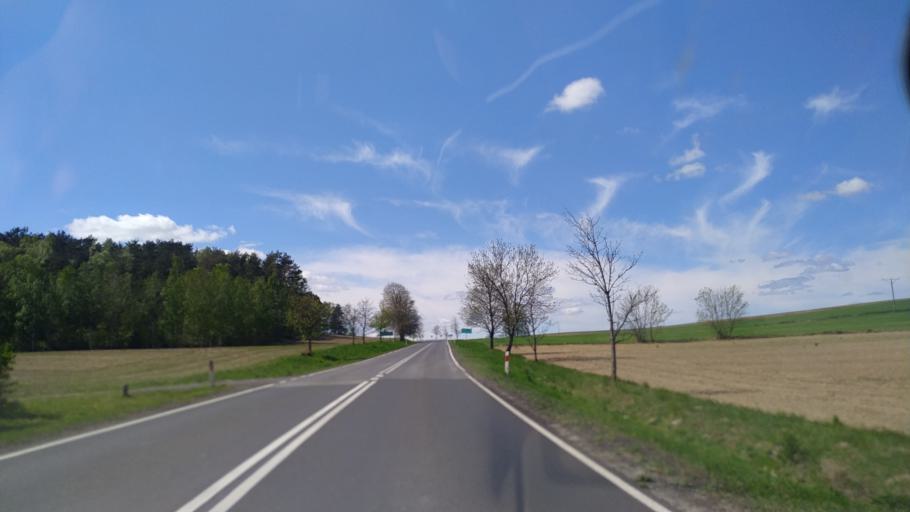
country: PL
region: Greater Poland Voivodeship
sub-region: Powiat pilski
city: Szydlowo
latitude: 53.2404
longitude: 16.6375
